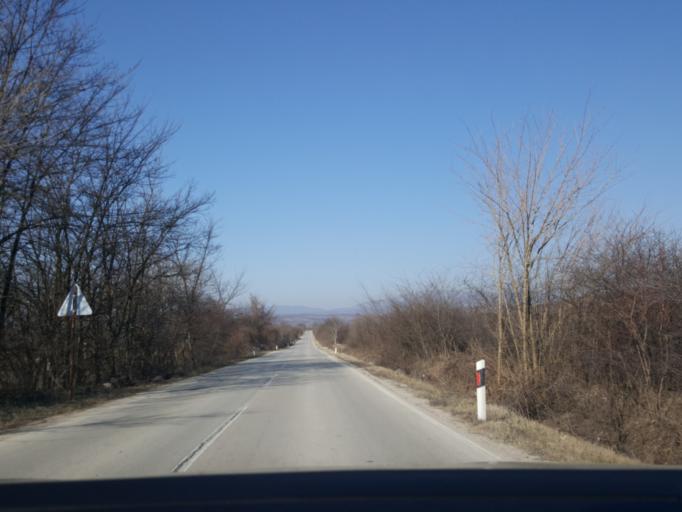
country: RS
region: Central Serbia
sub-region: Nisavski Okrug
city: Nis
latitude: 43.4105
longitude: 21.7973
